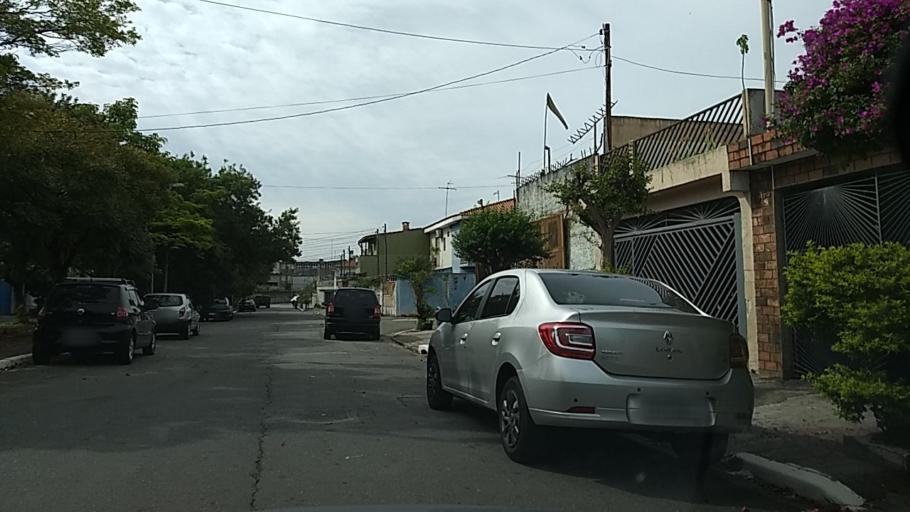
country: BR
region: Sao Paulo
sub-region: Guarulhos
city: Guarulhos
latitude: -23.4948
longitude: -46.5688
